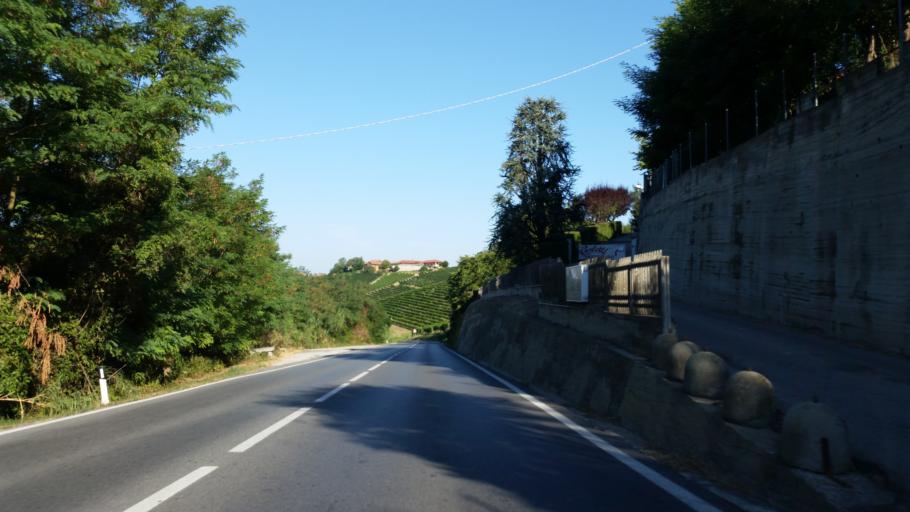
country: IT
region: Piedmont
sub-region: Provincia di Cuneo
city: Neive-Borgonovo
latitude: 44.7260
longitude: 8.1106
